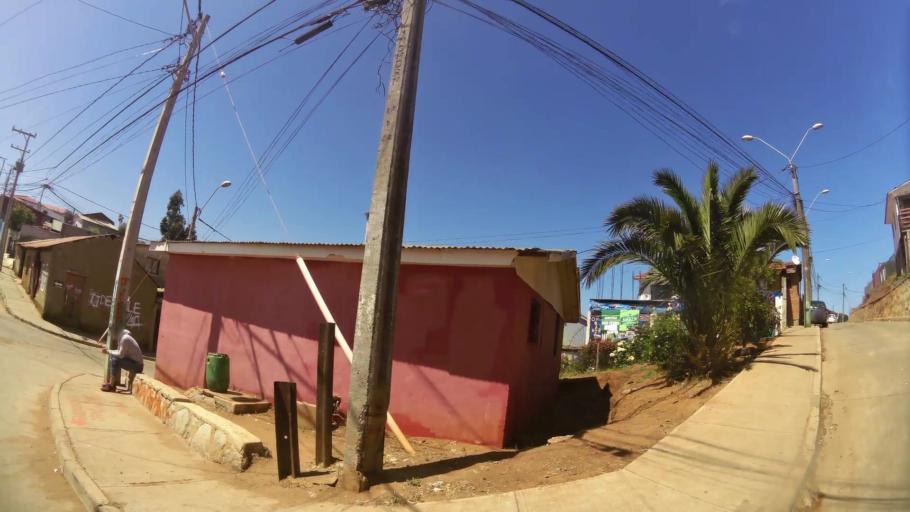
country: CL
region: Valparaiso
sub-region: Provincia de Valparaiso
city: Valparaiso
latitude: -33.0364
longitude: -71.6482
